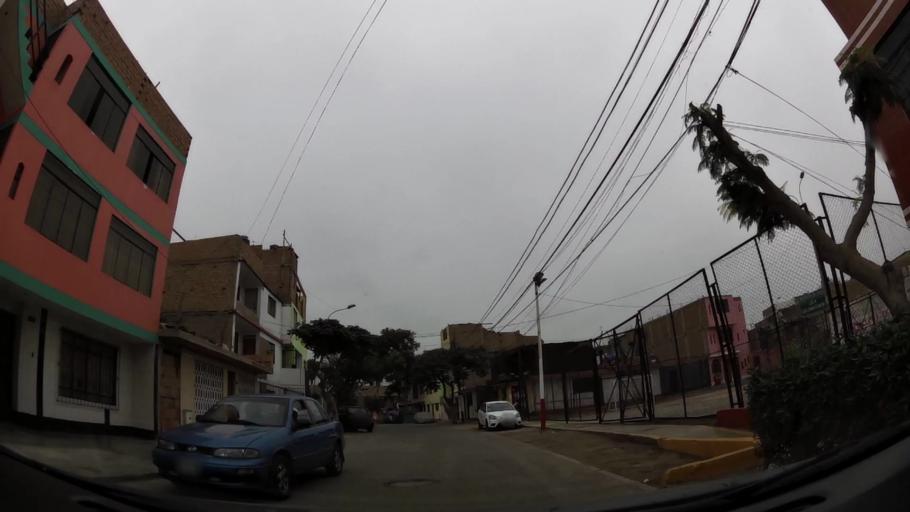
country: PE
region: Callao
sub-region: Callao
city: Callao
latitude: -12.0570
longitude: -77.1239
